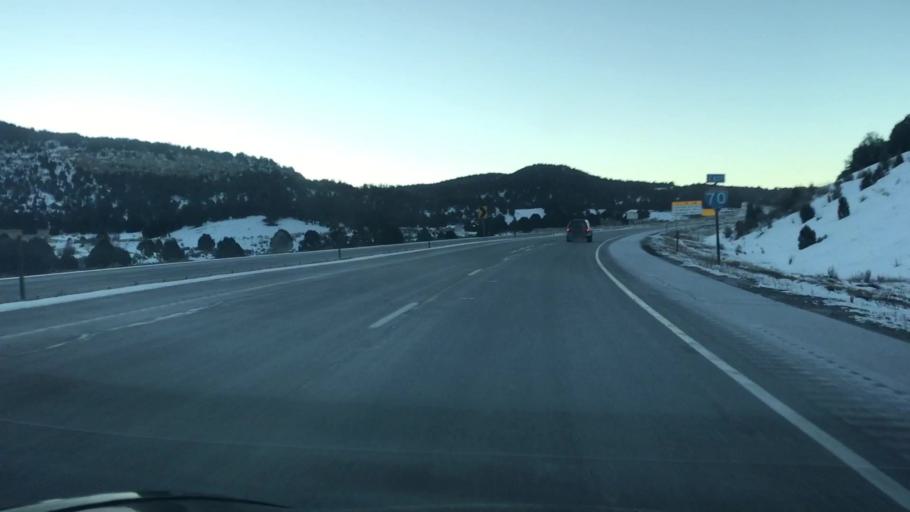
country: US
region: Utah
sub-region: Sevier County
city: Salina
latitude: 38.8746
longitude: -111.5545
